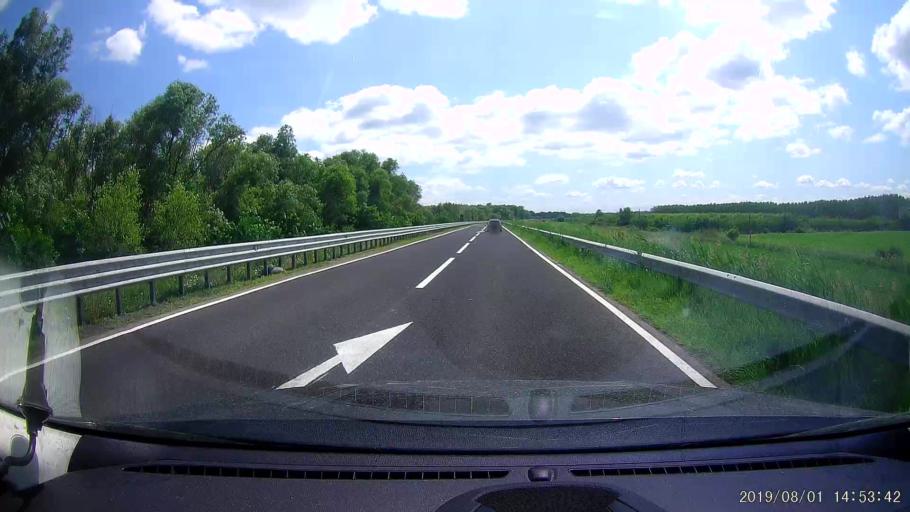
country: RO
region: Braila
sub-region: Municipiul Braila
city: Braila
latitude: 45.3301
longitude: 27.9994
